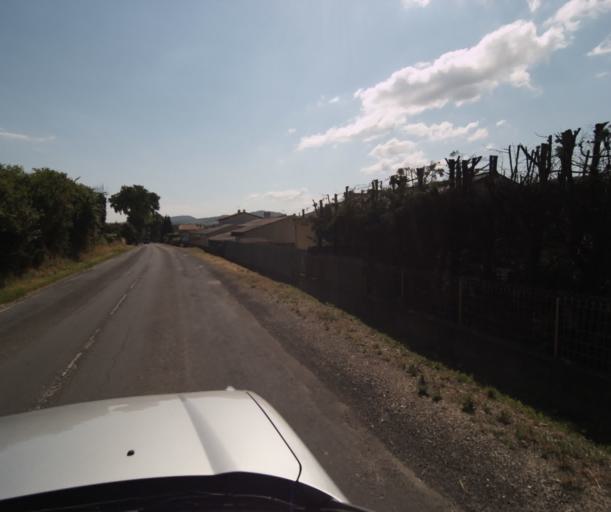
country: FR
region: Languedoc-Roussillon
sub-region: Departement de l'Aude
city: Limoux
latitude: 43.0538
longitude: 2.1991
